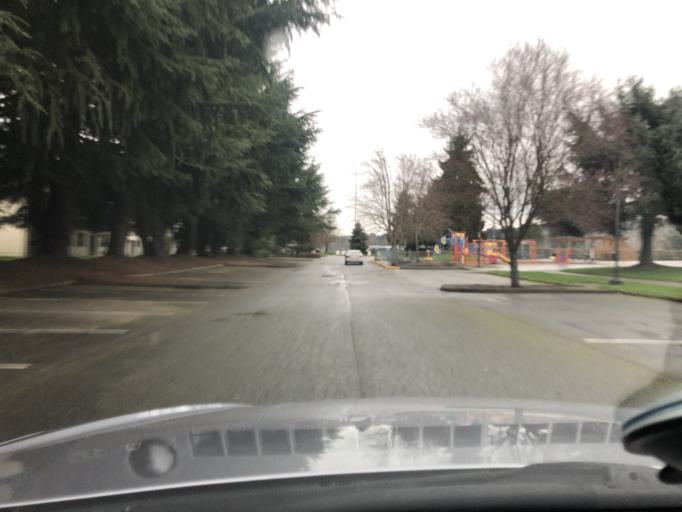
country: US
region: Washington
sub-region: King County
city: Auburn
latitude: 47.3308
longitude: -122.2149
